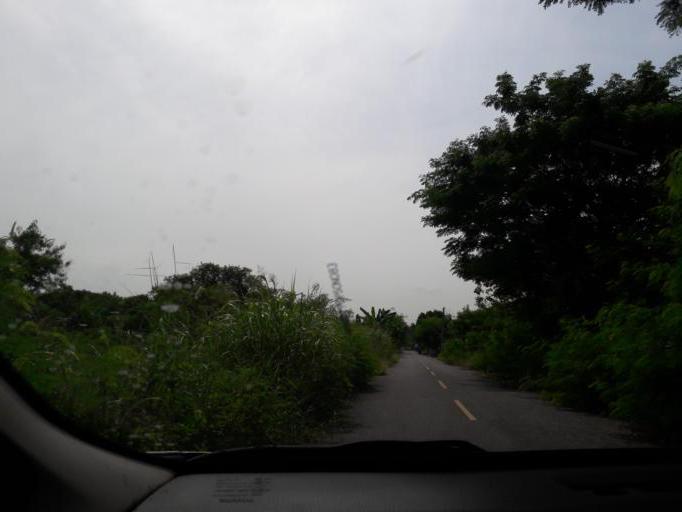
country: TH
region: Ang Thong
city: Ang Thong
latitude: 14.5795
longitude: 100.4542
